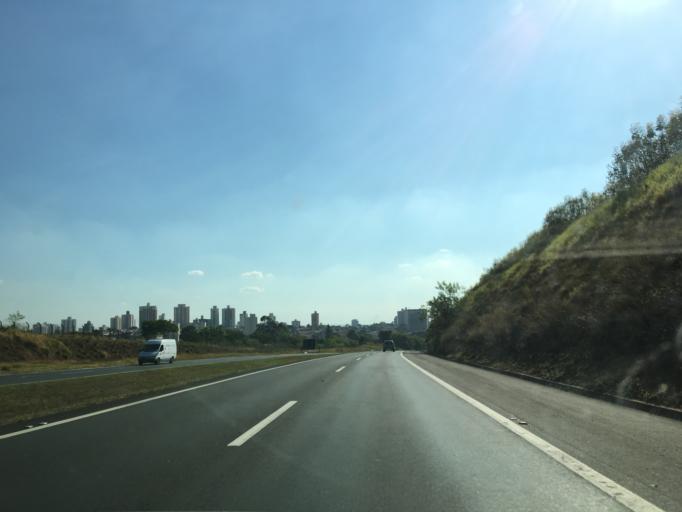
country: BR
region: Sao Paulo
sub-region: Piracicaba
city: Piracicaba
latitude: -22.7204
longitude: -47.6172
